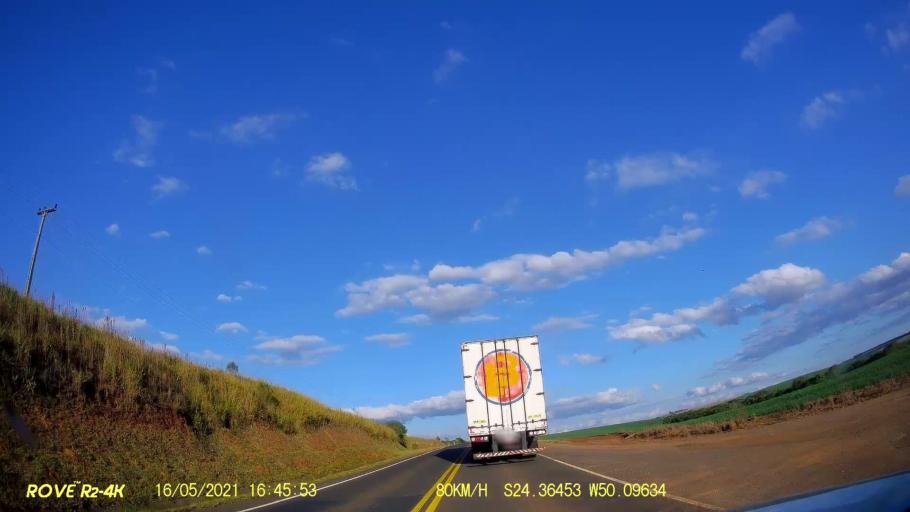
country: BR
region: Parana
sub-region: Pirai Do Sul
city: Pirai do Sul
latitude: -24.3617
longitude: -50.0978
